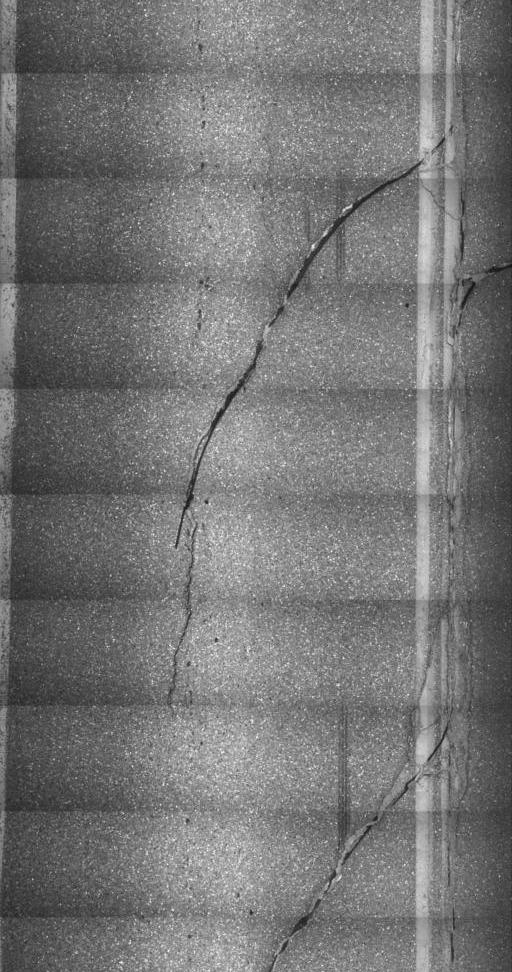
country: US
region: Vermont
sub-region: Addison County
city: Bristol
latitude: 44.2092
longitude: -72.9296
